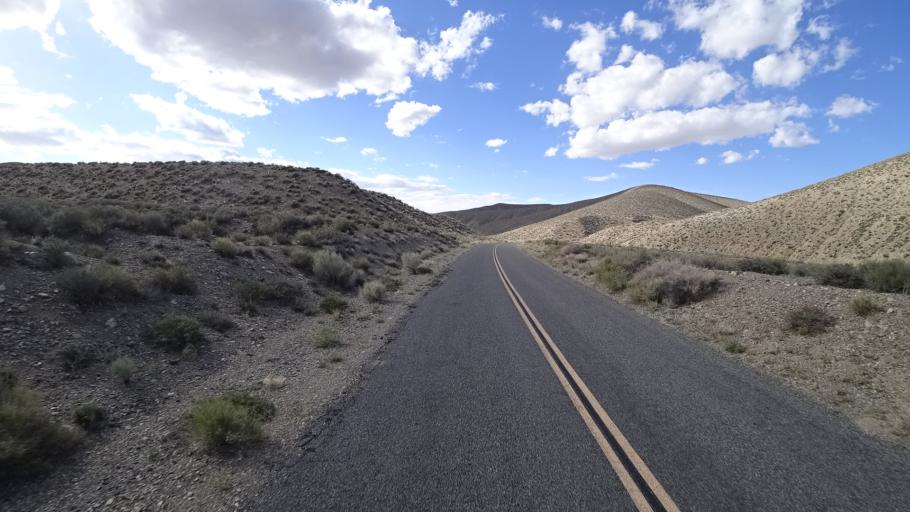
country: US
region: Nevada
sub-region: Nye County
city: Beatty
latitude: 36.3881
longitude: -117.1533
